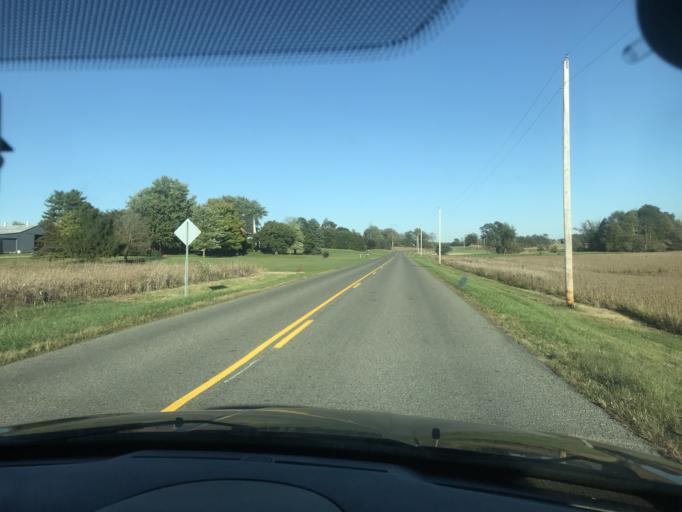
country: US
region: Ohio
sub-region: Logan County
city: De Graff
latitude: 40.3233
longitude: -83.8789
